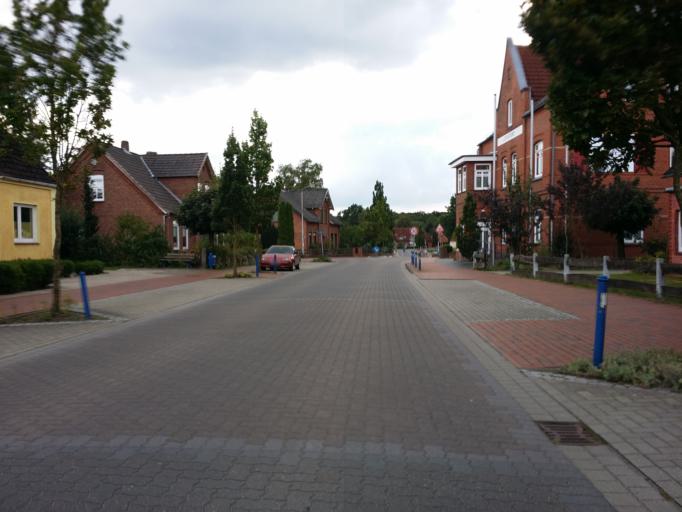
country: DE
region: Lower Saxony
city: Hemmoor
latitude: 53.6847
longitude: 9.1681
